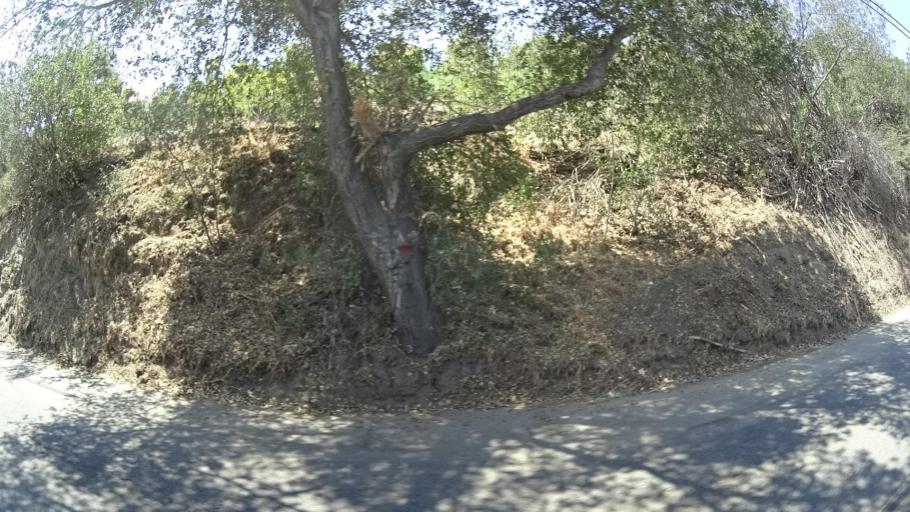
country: US
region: California
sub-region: San Diego County
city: Fallbrook
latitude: 33.4287
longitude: -117.3075
